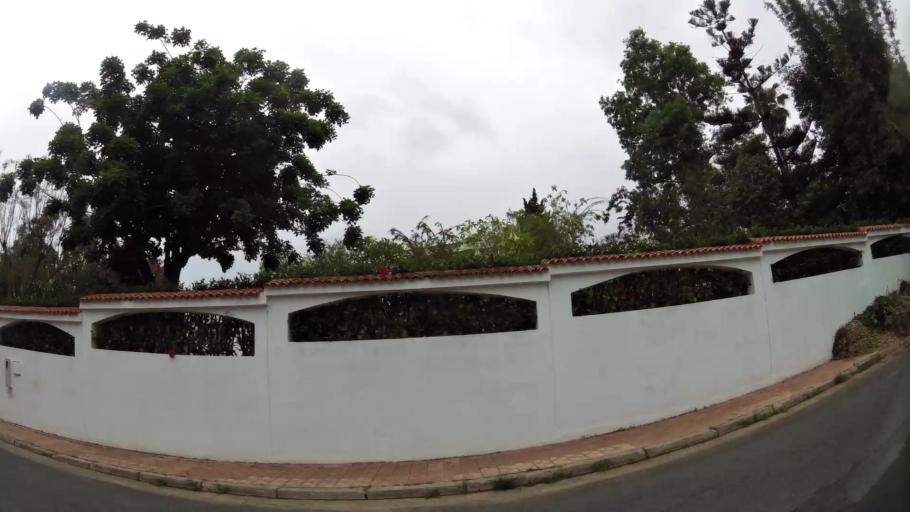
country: MA
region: Rabat-Sale-Zemmour-Zaer
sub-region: Rabat
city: Rabat
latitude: 33.9605
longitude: -6.8129
